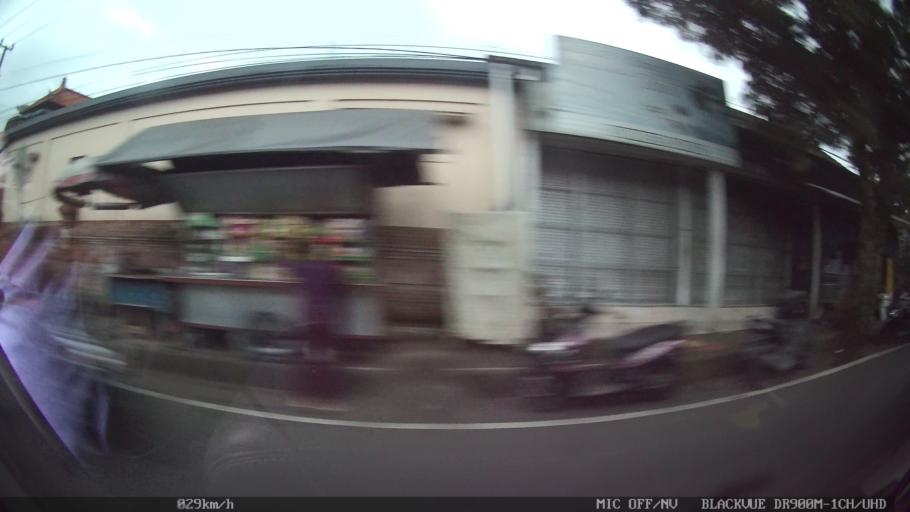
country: ID
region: Bali
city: Badung
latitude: -8.4336
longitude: 115.2452
